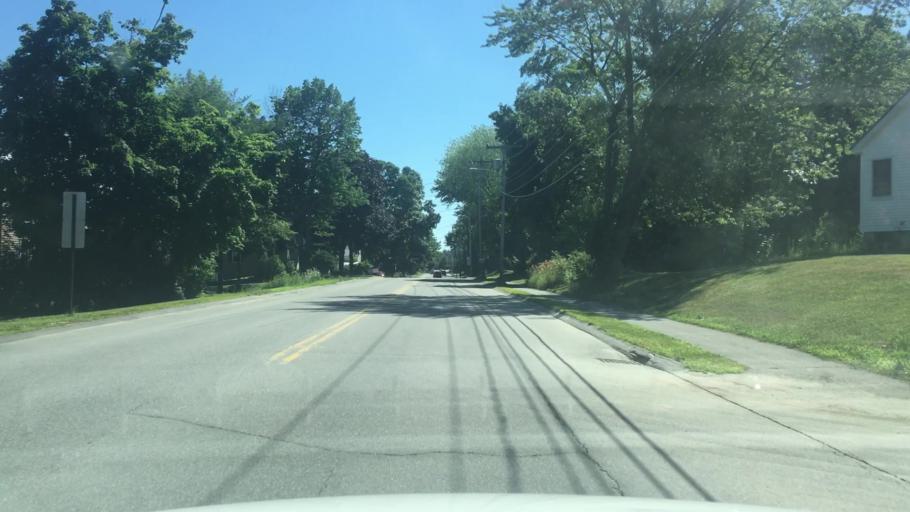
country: US
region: Maine
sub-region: Kennebec County
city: Waterville
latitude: 44.5454
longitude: -69.6459
